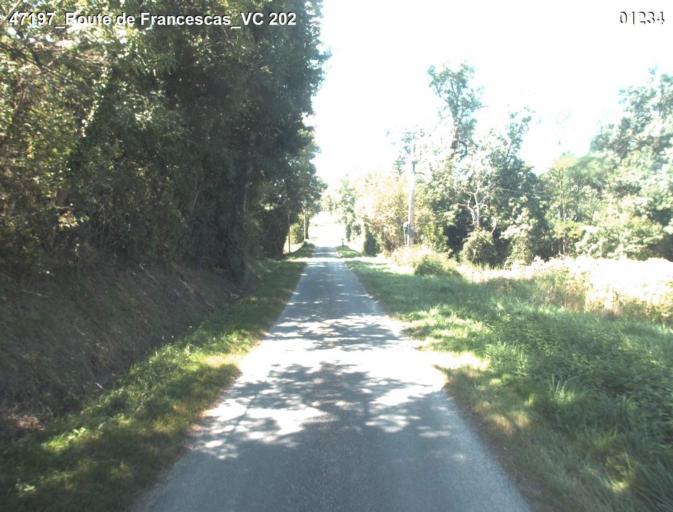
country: FR
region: Aquitaine
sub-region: Departement du Lot-et-Garonne
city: Laplume
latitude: 44.0714
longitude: 0.4624
